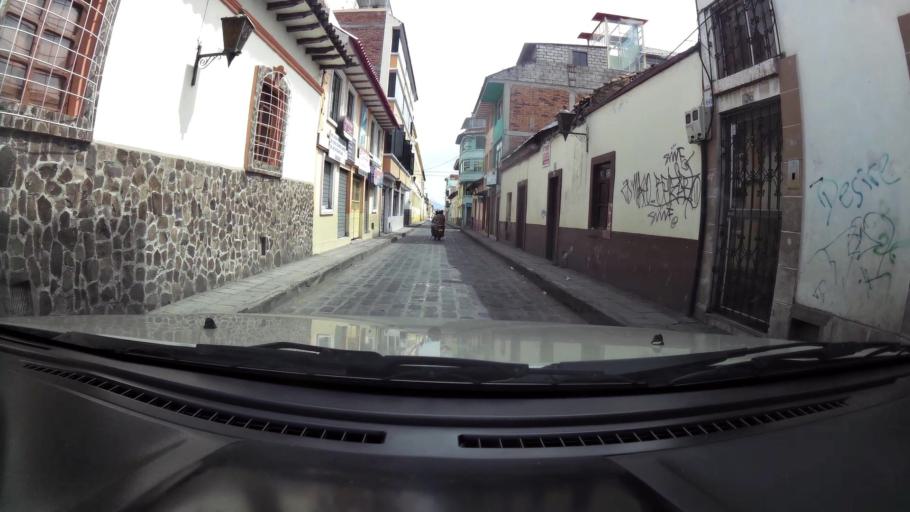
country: EC
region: Cotopaxi
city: Latacunga
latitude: -0.9319
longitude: -78.6078
